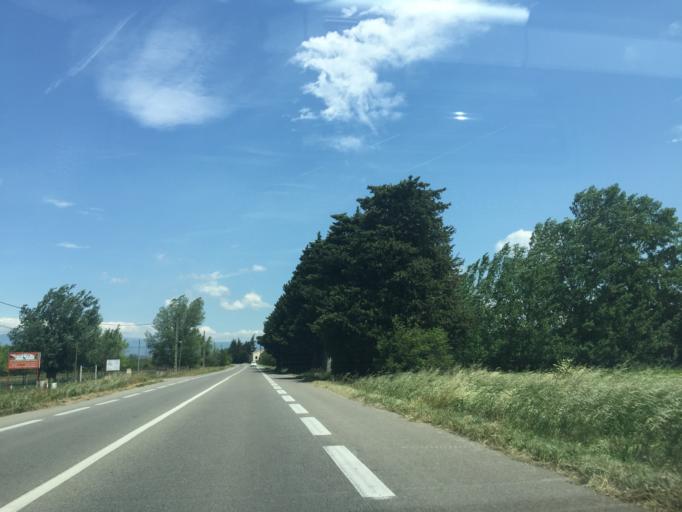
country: FR
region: Provence-Alpes-Cote d'Azur
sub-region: Departement du Vaucluse
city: Velleron
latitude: 43.9834
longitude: 5.0215
